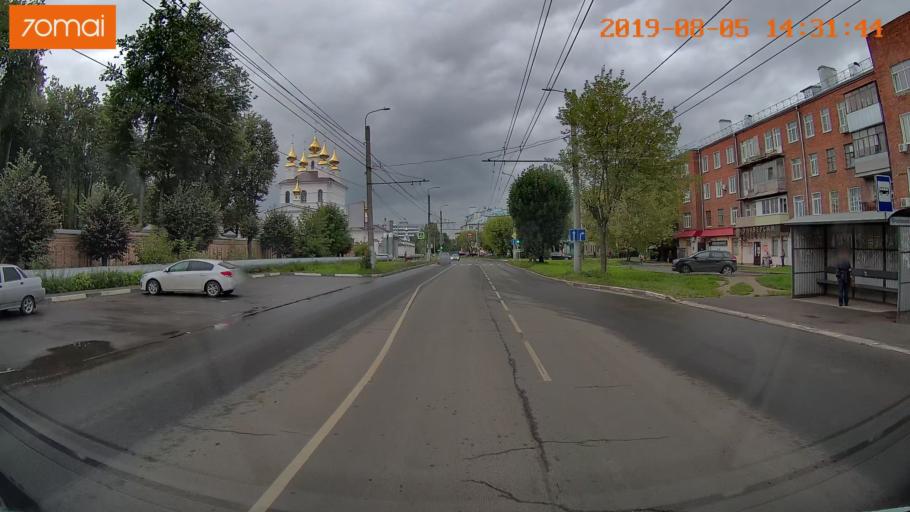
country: RU
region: Ivanovo
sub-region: Gorod Ivanovo
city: Ivanovo
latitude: 56.9884
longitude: 40.9980
